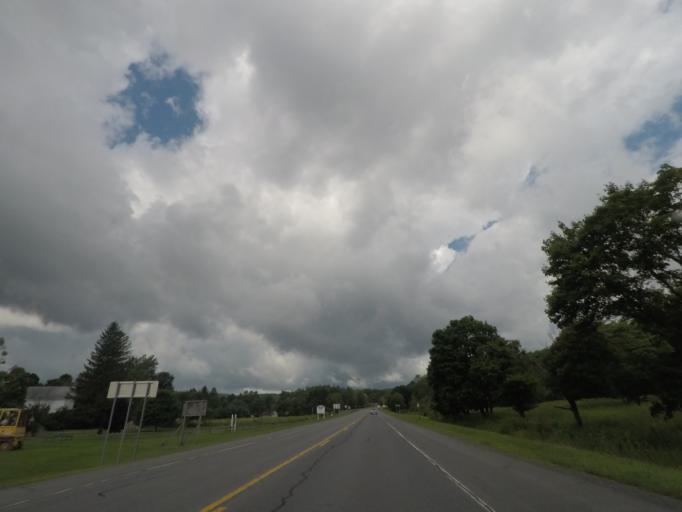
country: US
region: Massachusetts
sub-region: Berkshire County
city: Lanesborough
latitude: 42.5486
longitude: -73.3699
